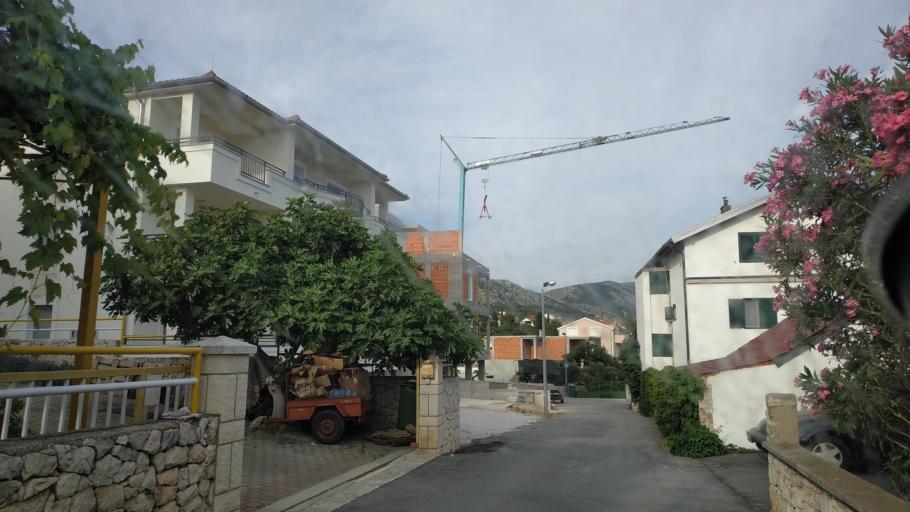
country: HR
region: Sibensko-Kniniska
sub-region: Grad Sibenik
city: Brodarica
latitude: 43.6367
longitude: 15.9609
